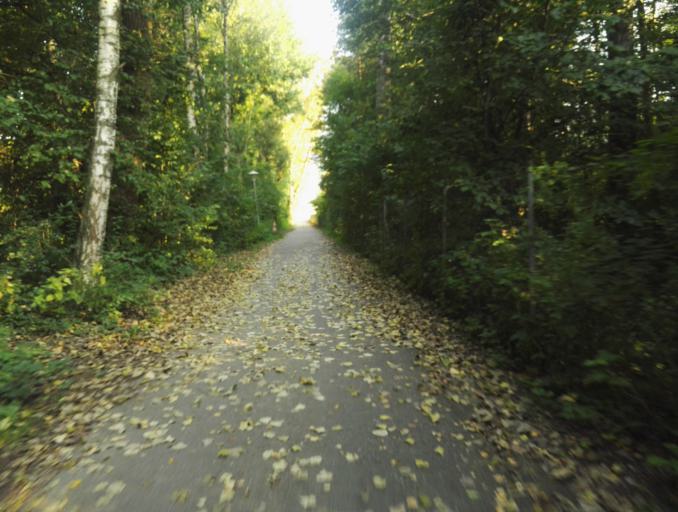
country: AT
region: Styria
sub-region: Politischer Bezirk Graz-Umgebung
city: Gratkorn
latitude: 47.1247
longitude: 15.3448
